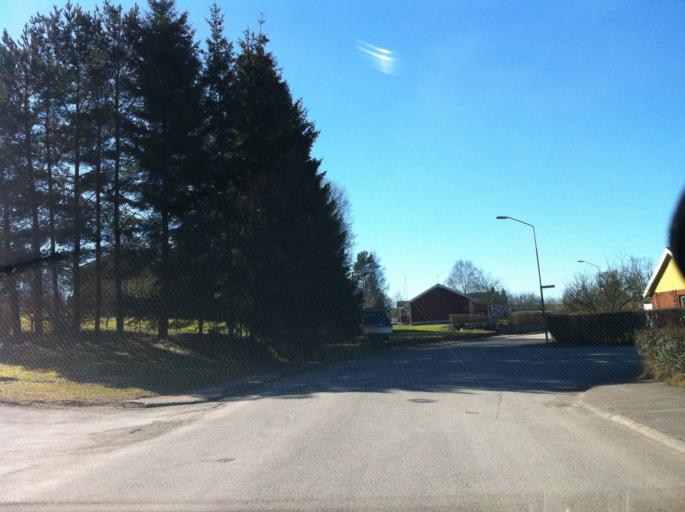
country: SE
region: Vaestra Goetaland
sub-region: Vanersborgs Kommun
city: Vargon
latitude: 58.3709
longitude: 12.4322
